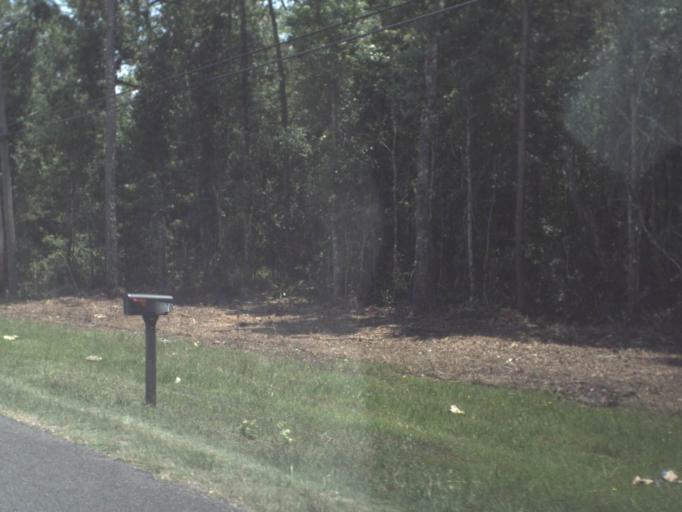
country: US
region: Florida
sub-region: Clay County
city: Green Cove Springs
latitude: 29.9880
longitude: -81.5729
